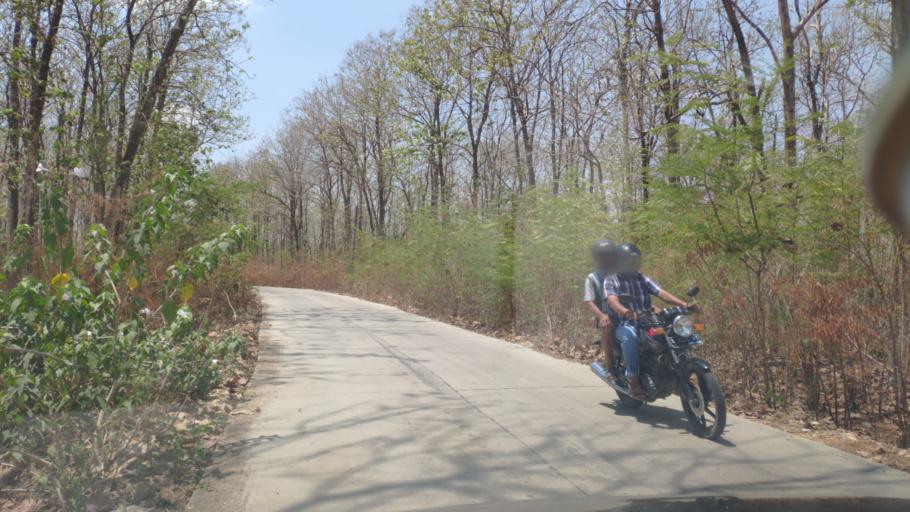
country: ID
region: Central Java
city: Randublatung
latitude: -7.2578
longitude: 111.3775
